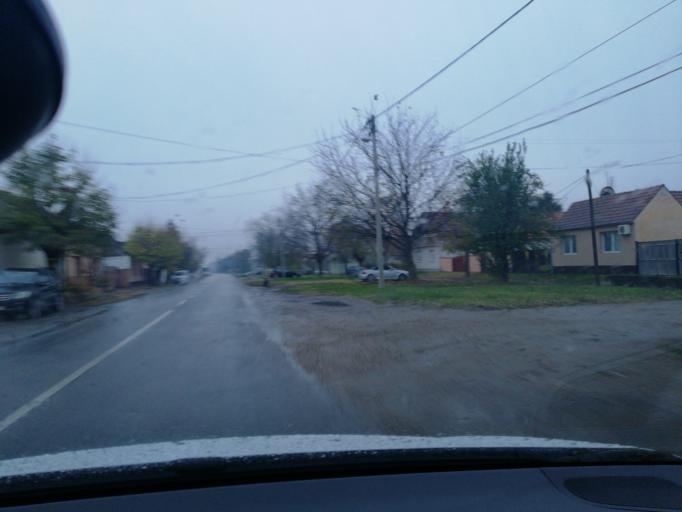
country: RS
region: Autonomna Pokrajina Vojvodina
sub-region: Sremski Okrug
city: Ruma
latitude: 45.0012
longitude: 19.8159
